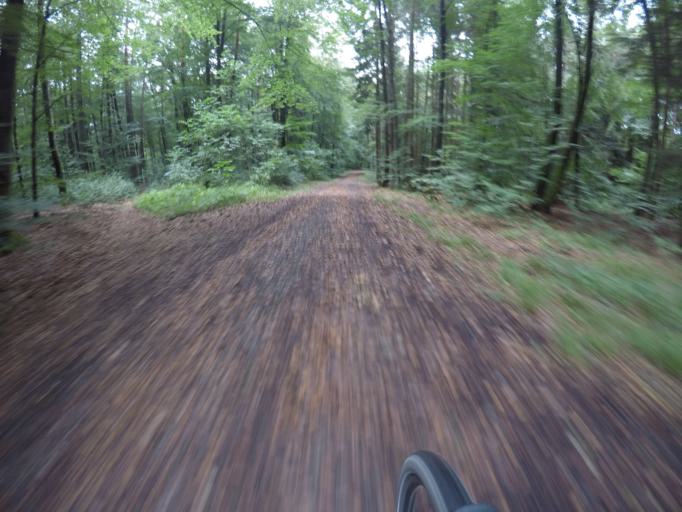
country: DE
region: Baden-Wuerttemberg
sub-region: Regierungsbezirk Stuttgart
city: Steinenbronn
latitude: 48.7258
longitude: 9.0842
